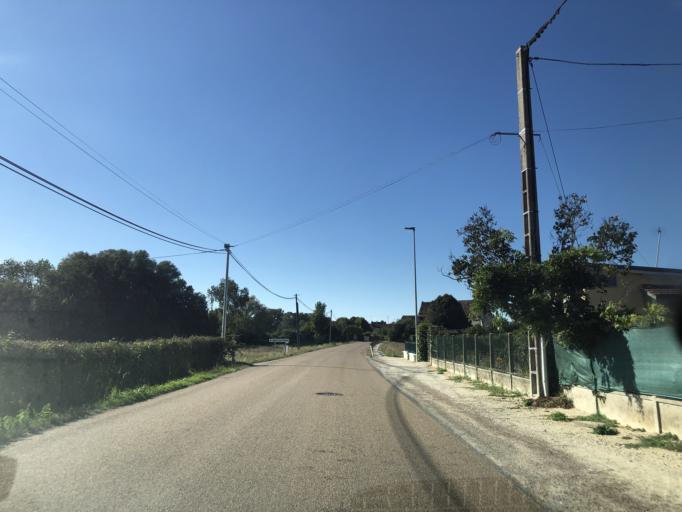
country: FR
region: Bourgogne
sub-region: Departement de l'Yonne
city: Cheny
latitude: 47.9247
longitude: 3.5242
